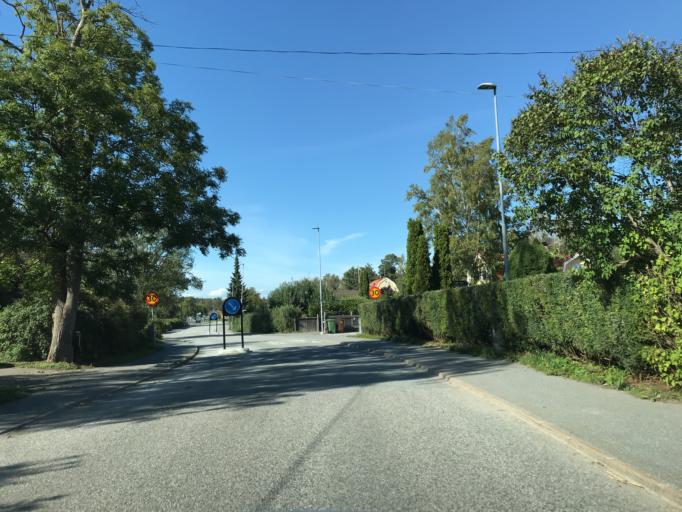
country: SE
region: Stockholm
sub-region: Sollentuna Kommun
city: Sollentuna
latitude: 59.4224
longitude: 17.9326
